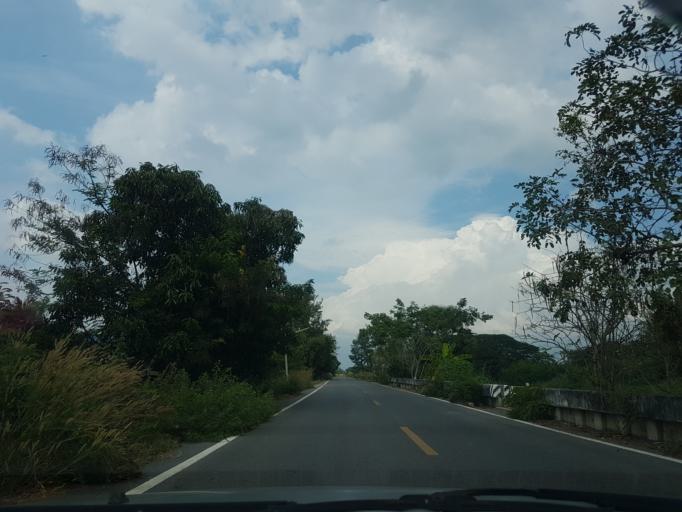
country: TH
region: Sara Buri
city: Nong Khae
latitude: 14.2576
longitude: 100.8913
